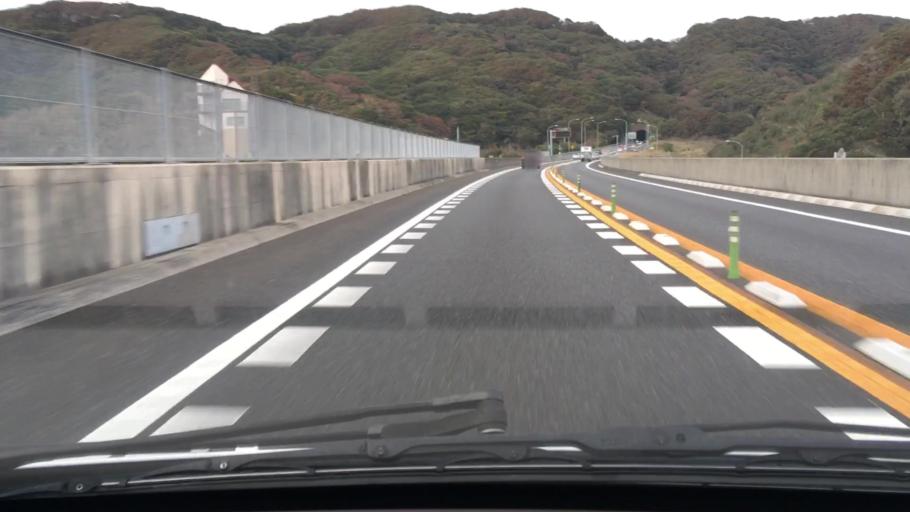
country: JP
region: Chiba
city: Futtsu
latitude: 35.1694
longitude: 139.8303
